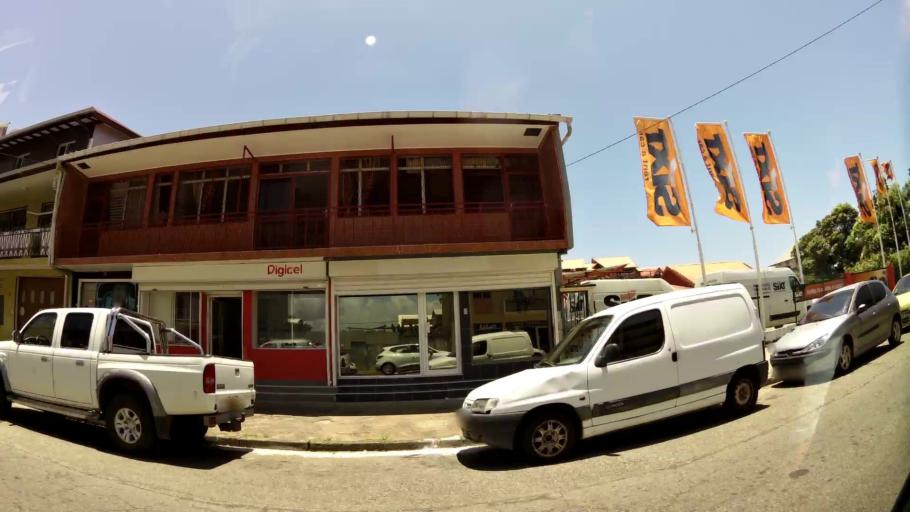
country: GF
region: Guyane
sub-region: Guyane
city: Cayenne
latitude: 4.9370
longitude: -52.3307
